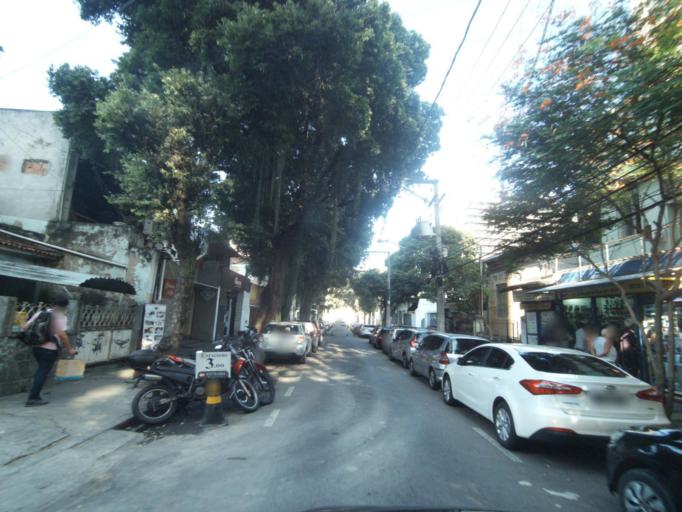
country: BR
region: Rio de Janeiro
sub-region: Niteroi
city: Niteroi
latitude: -22.8918
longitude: -43.1197
